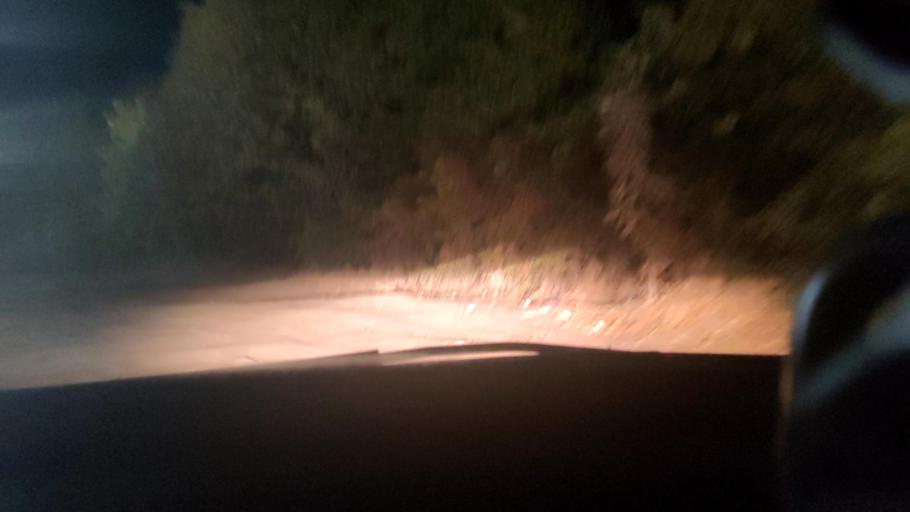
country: RU
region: Voronezj
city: Voronezh
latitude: 51.7282
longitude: 39.2120
